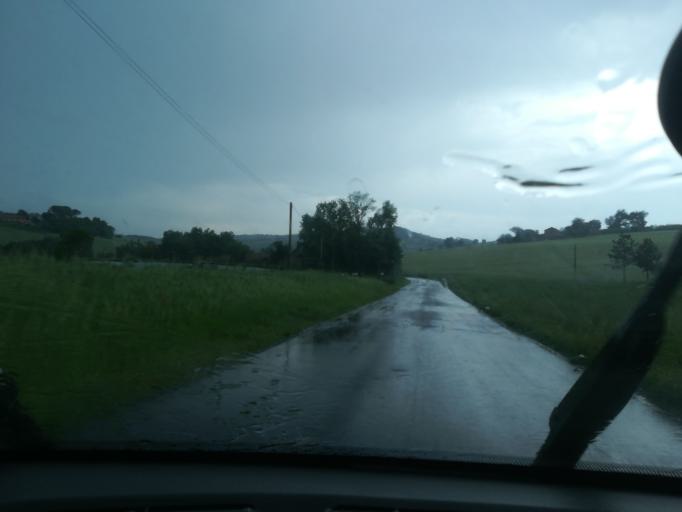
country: IT
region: The Marches
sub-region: Provincia di Macerata
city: Passo di Treia
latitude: 43.3039
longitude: 13.3441
